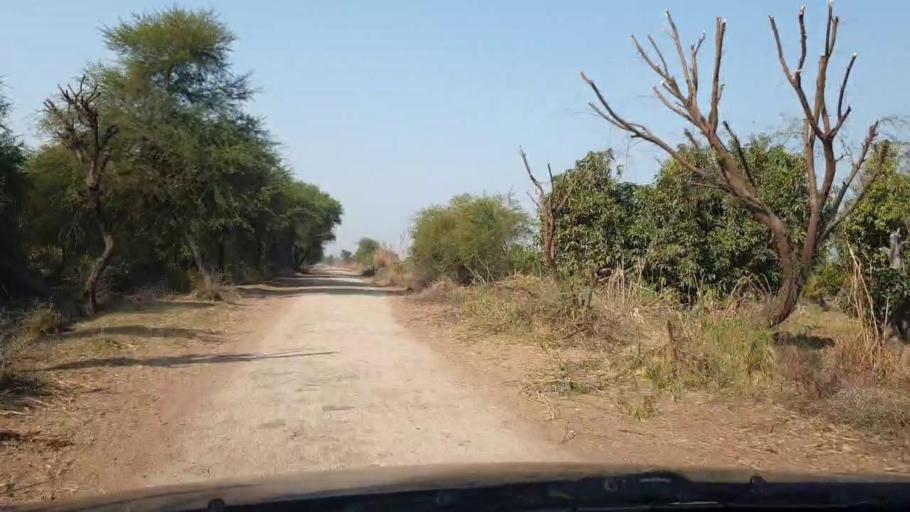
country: PK
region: Sindh
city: Jhol
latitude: 25.9613
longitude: 68.9714
